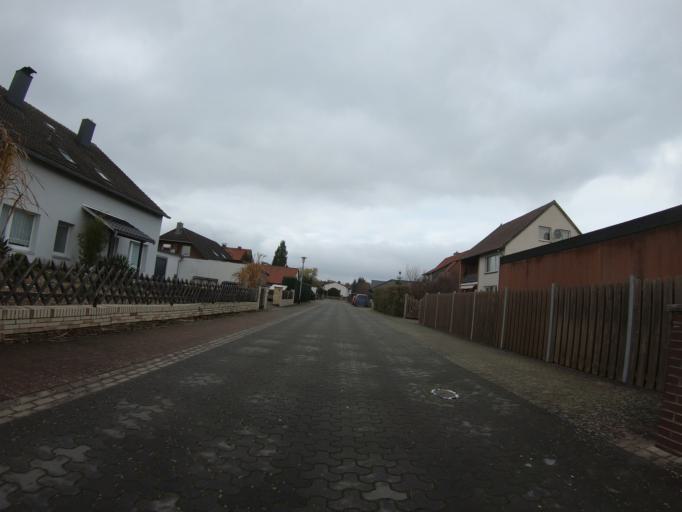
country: DE
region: Lower Saxony
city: Wagenhoff
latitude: 52.5531
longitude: 10.5200
